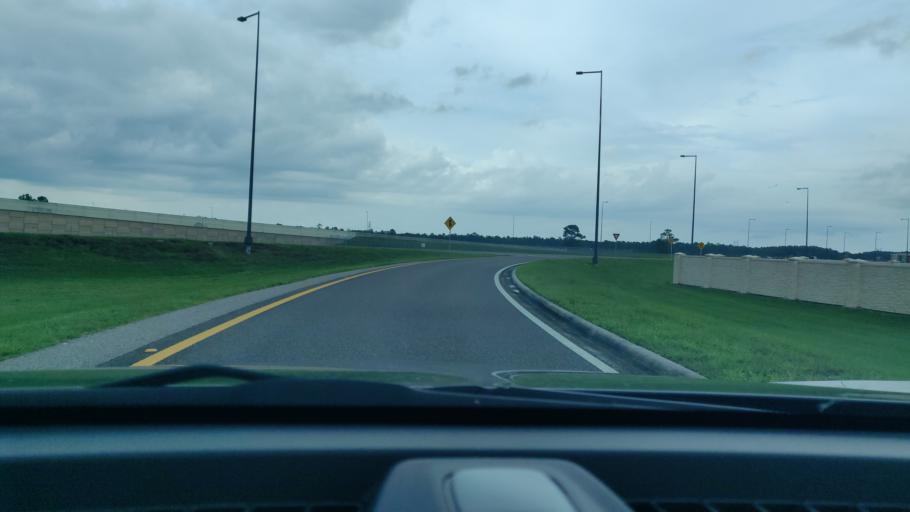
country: US
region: Florida
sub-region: Osceola County
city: Celebration
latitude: 28.3398
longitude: -81.4807
